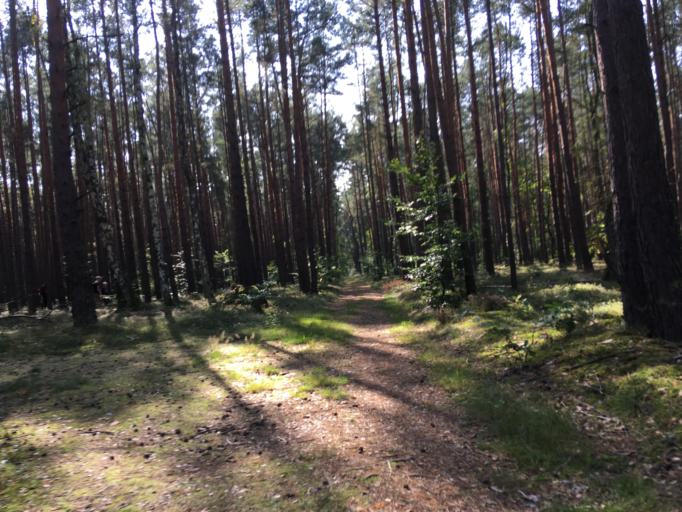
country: DE
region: Brandenburg
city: Wandlitz
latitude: 52.6968
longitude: 13.4372
